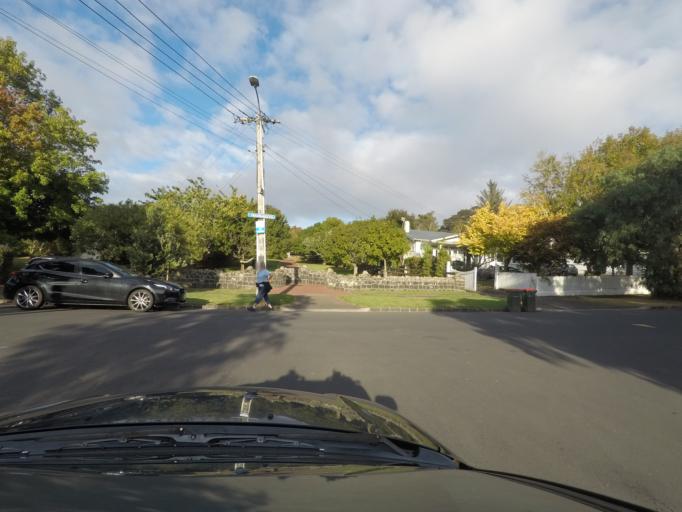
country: NZ
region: Auckland
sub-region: Auckland
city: Auckland
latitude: -36.8951
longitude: 174.7923
